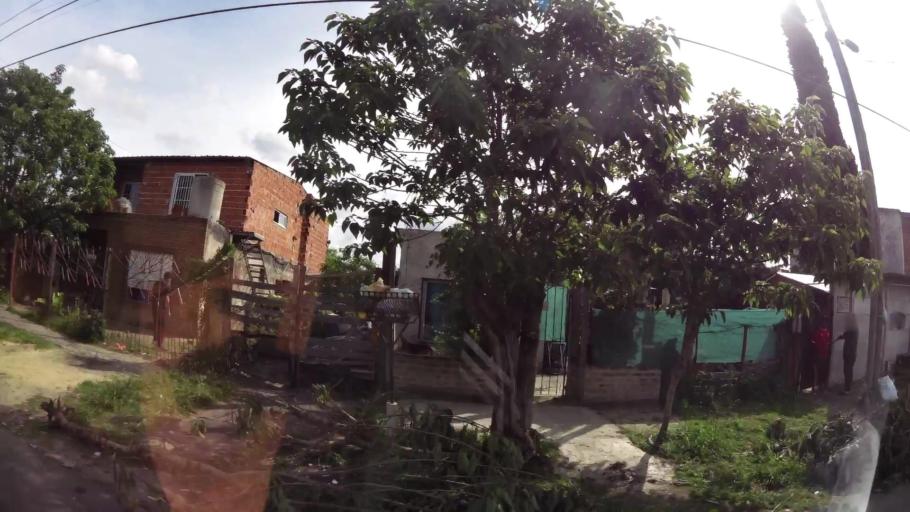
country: AR
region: Buenos Aires
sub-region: Partido de Quilmes
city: Quilmes
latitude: -34.7734
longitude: -58.2554
